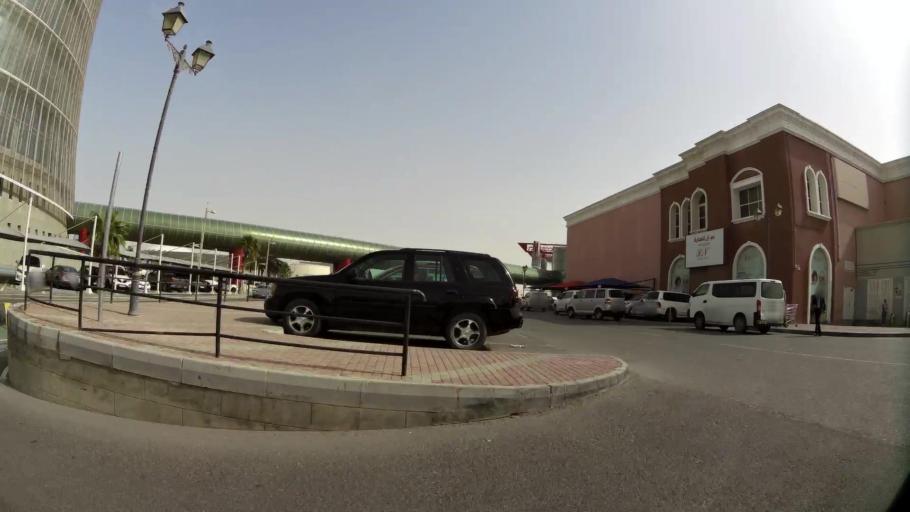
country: QA
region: Baladiyat ar Rayyan
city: Ar Rayyan
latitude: 25.2623
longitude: 51.4440
